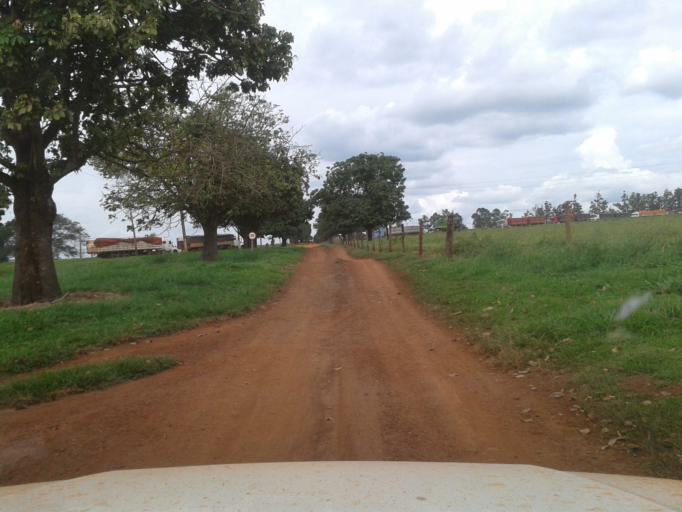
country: BR
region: Minas Gerais
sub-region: Centralina
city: Centralina
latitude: -18.7738
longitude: -49.2267
